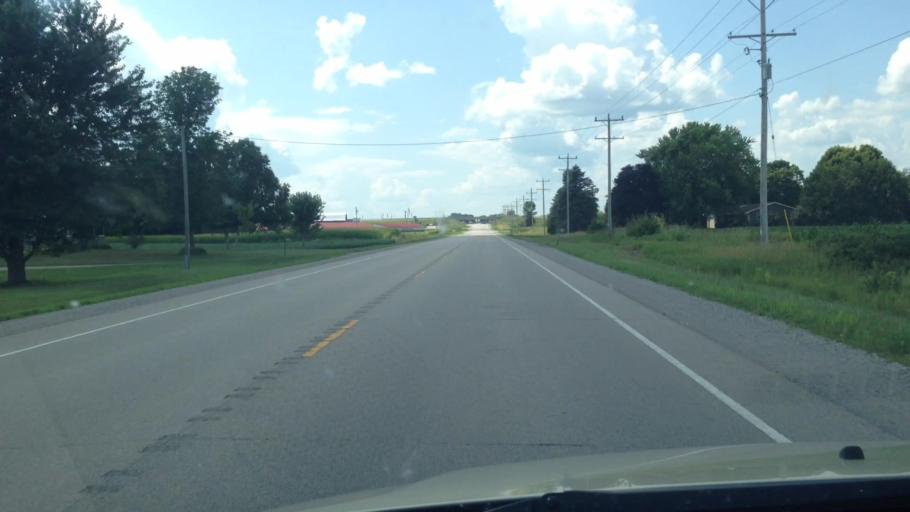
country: US
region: Wisconsin
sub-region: Brown County
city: Pulaski
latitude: 44.6736
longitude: -88.2970
